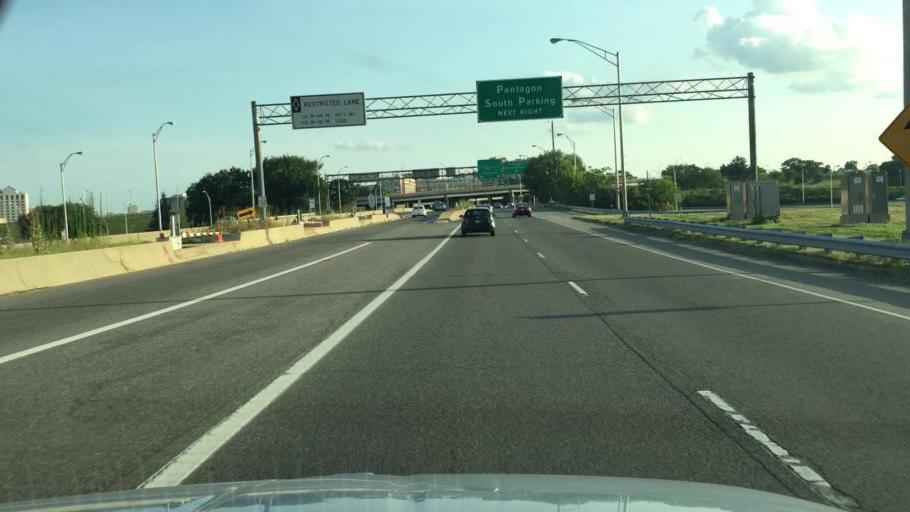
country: US
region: Washington, D.C.
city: Washington, D.C.
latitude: 38.8709
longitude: -77.0603
